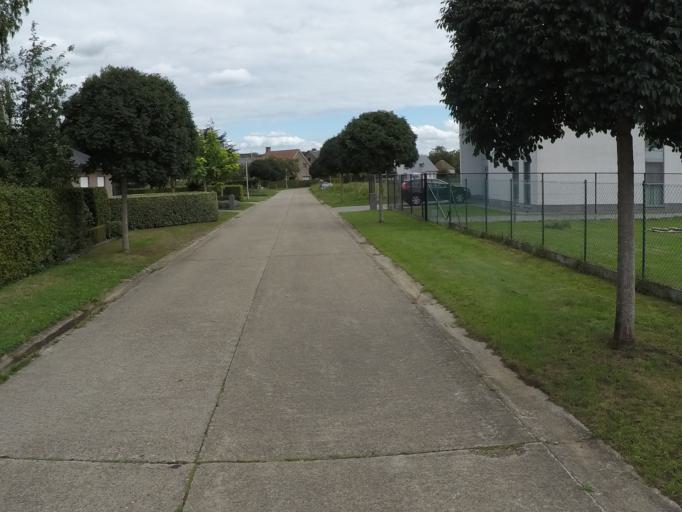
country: BE
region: Flanders
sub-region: Provincie Antwerpen
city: Zandhoven
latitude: 51.2174
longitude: 4.6687
